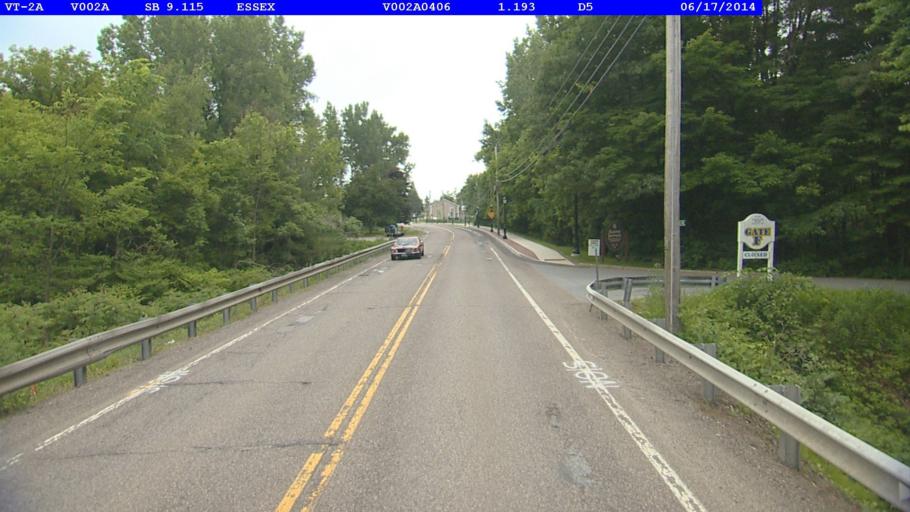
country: US
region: Vermont
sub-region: Chittenden County
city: Essex Junction
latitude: 44.4979
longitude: -73.1129
